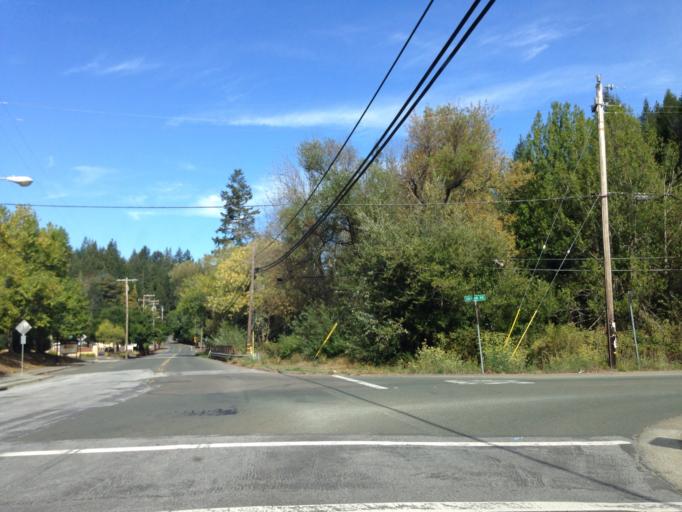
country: US
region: California
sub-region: Sonoma County
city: Occidental
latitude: 38.4102
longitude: -122.9491
